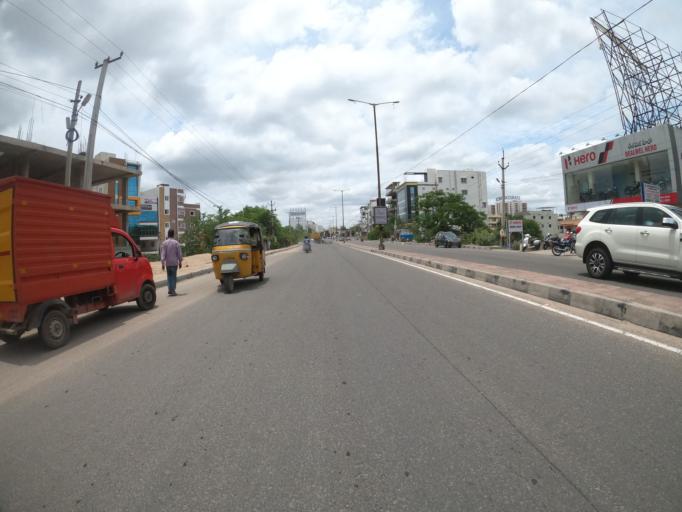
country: IN
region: Telangana
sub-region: Hyderabad
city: Hyderabad
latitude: 17.3851
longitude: 78.3575
